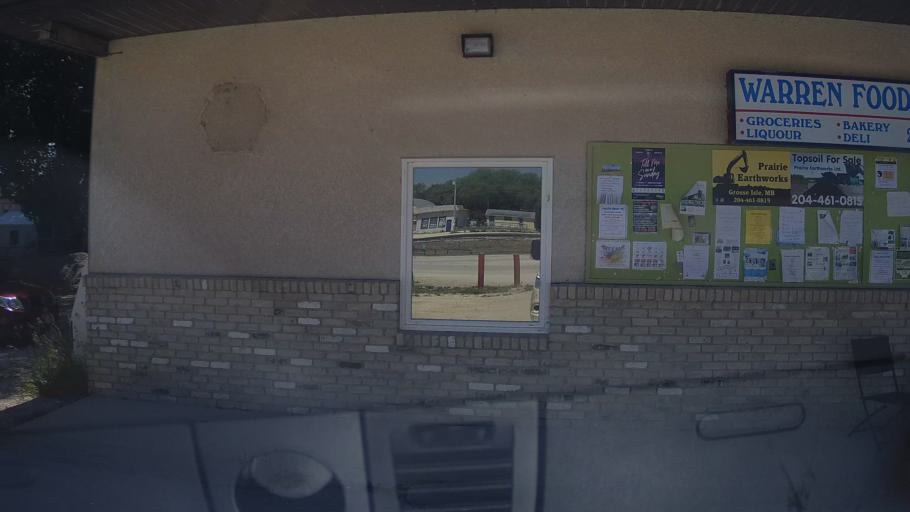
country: CA
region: Manitoba
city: Stonewall
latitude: 50.1303
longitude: -97.5444
